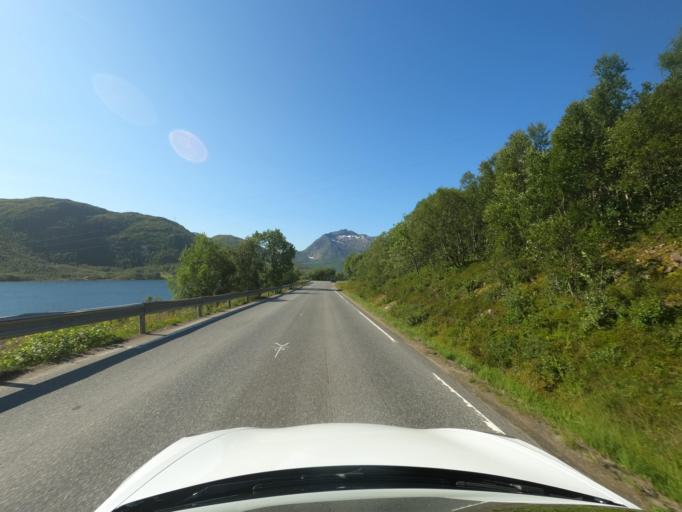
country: NO
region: Nordland
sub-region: Lodingen
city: Lodingen
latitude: 68.5648
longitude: 15.8004
